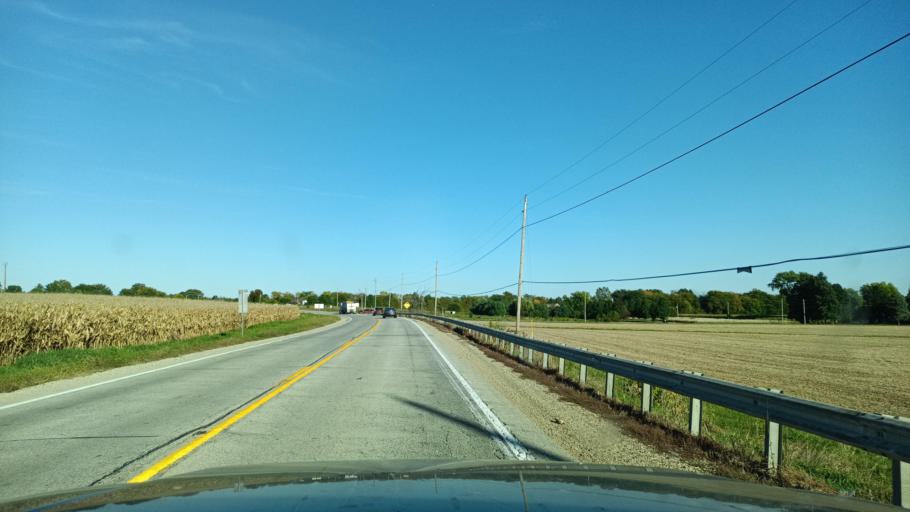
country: US
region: Illinois
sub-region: De Witt County
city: Farmer City
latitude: 40.2323
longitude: -88.6632
